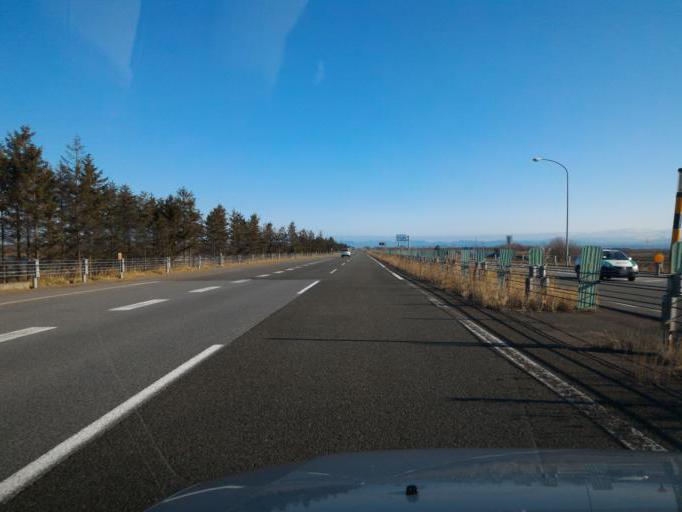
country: JP
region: Hokkaido
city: Ebetsu
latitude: 43.1062
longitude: 141.6027
